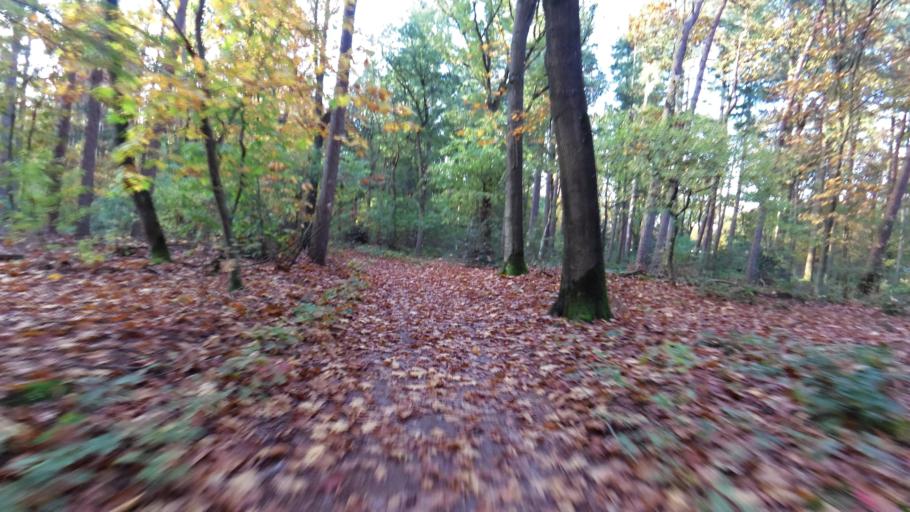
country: NL
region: Gelderland
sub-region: Gemeente Ede
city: Lunteren
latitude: 52.0893
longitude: 5.6416
